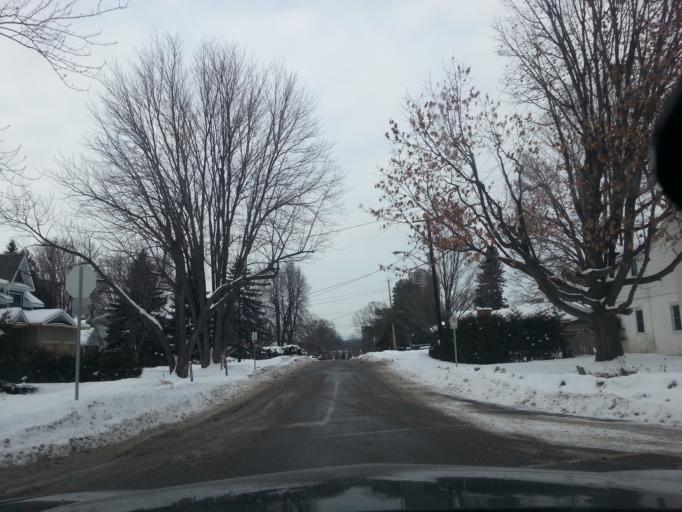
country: CA
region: Ontario
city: Bells Corners
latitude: 45.3709
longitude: -75.7761
